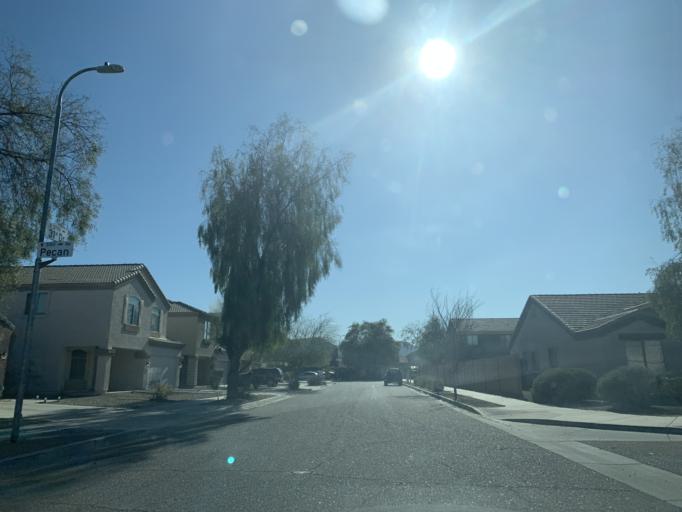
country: US
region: Arizona
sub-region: Maricopa County
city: Laveen
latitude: 33.3952
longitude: -112.1258
